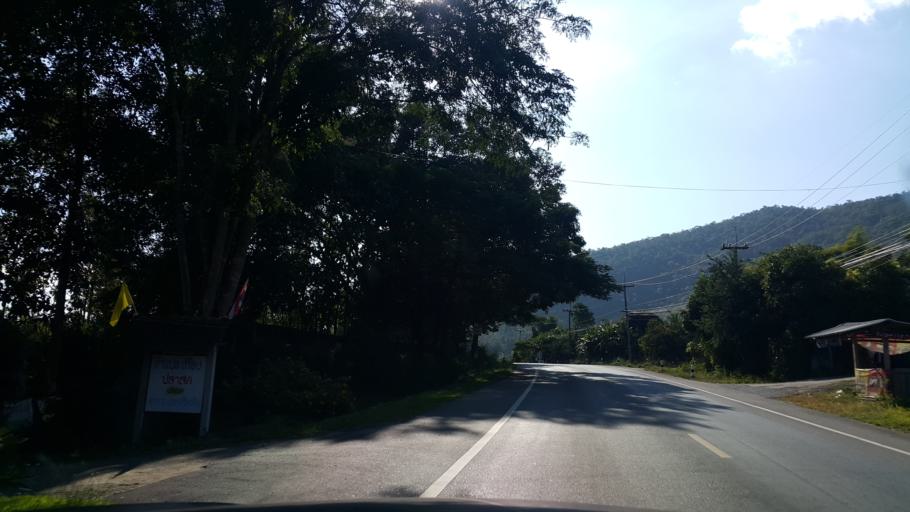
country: TH
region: Lamphun
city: Mae Tha
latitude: 18.4913
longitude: 99.1872
